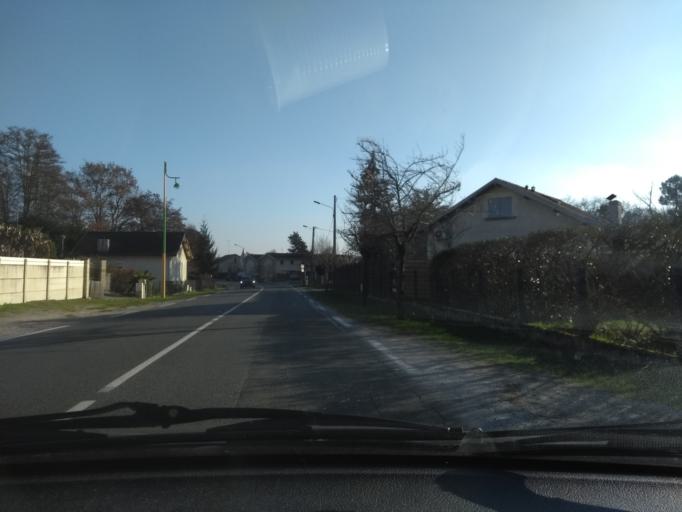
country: FR
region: Aquitaine
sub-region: Departement de la Gironde
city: Mios
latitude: 44.6085
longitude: -0.9429
